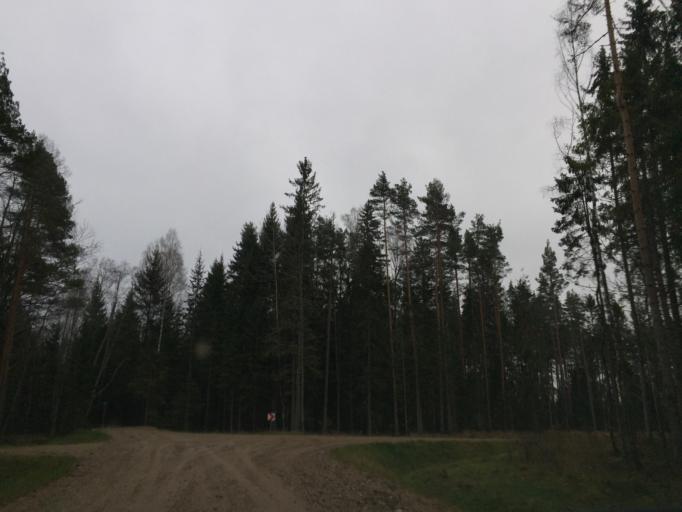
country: LV
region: Burtnieki
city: Matisi
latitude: 57.5412
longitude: 25.1627
